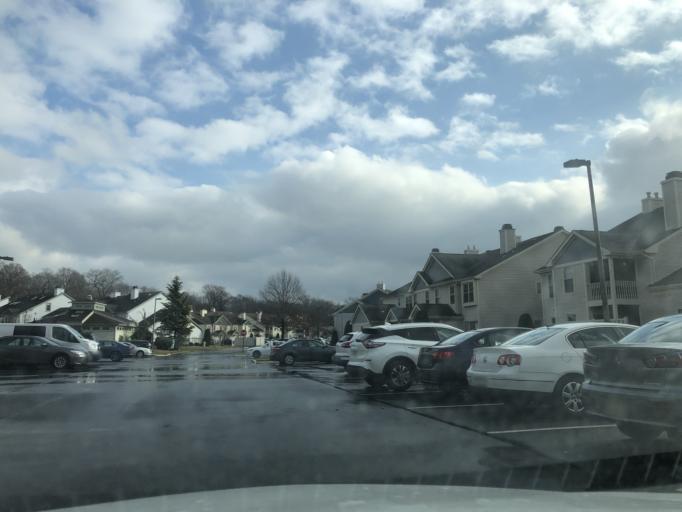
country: US
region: New Jersey
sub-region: Camden County
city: Bellmawr
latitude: 39.8457
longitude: -75.1072
